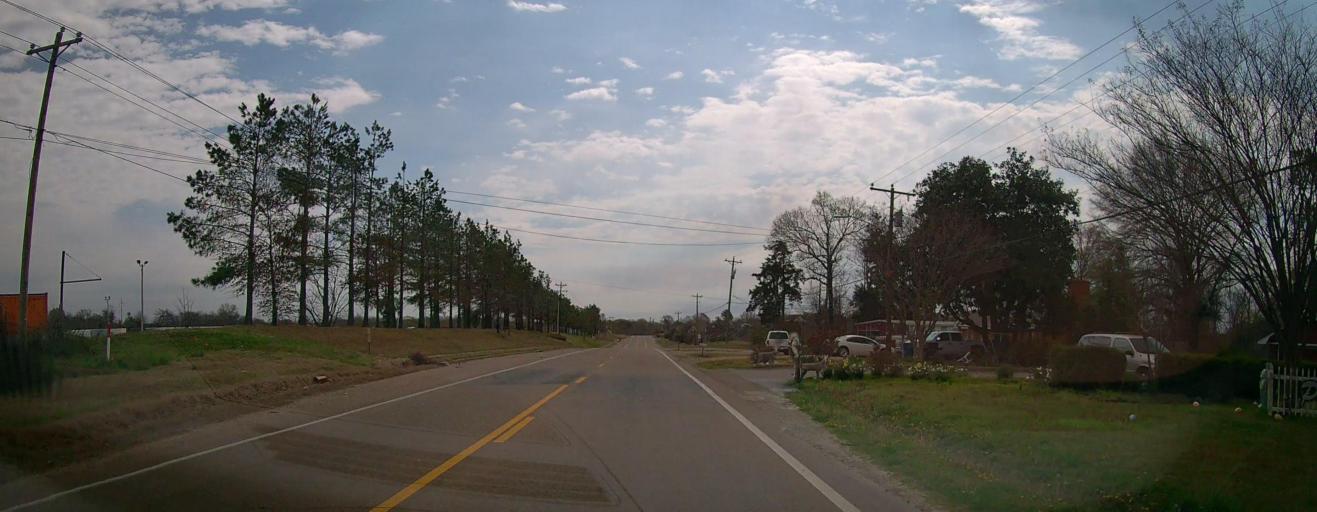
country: US
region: Mississippi
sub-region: De Soto County
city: Olive Branch
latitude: 34.9796
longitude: -89.8537
